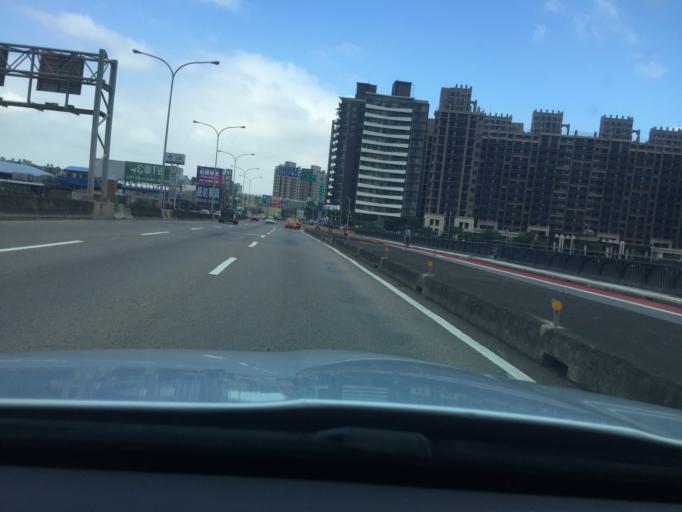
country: TW
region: Taiwan
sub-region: Hsinchu
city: Zhubei
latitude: 24.8238
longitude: 120.9968
